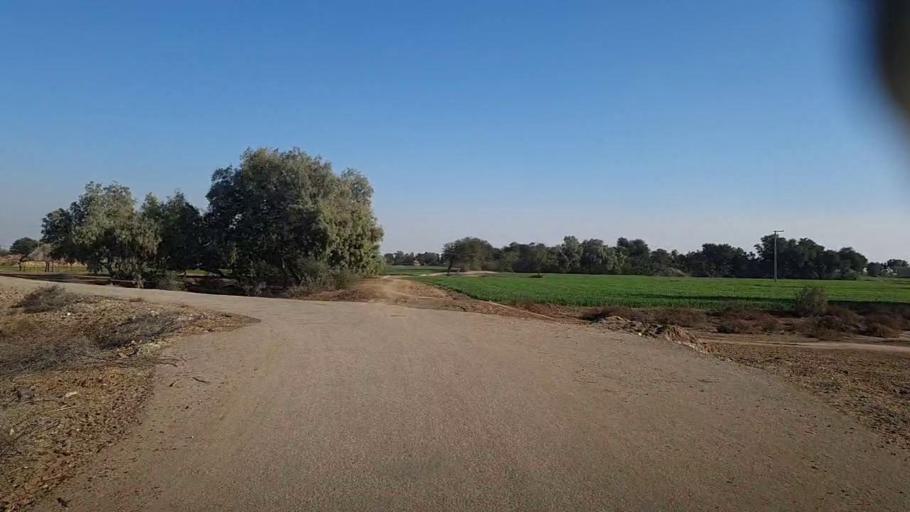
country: PK
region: Sindh
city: Khairpur
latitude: 27.8928
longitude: 69.7534
